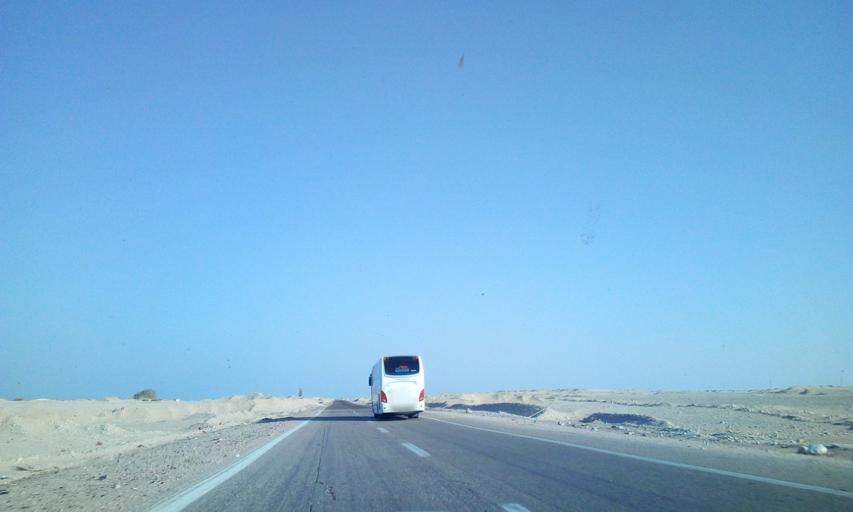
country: EG
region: As Suways
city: Ain Sukhna
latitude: 28.8609
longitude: 32.6786
